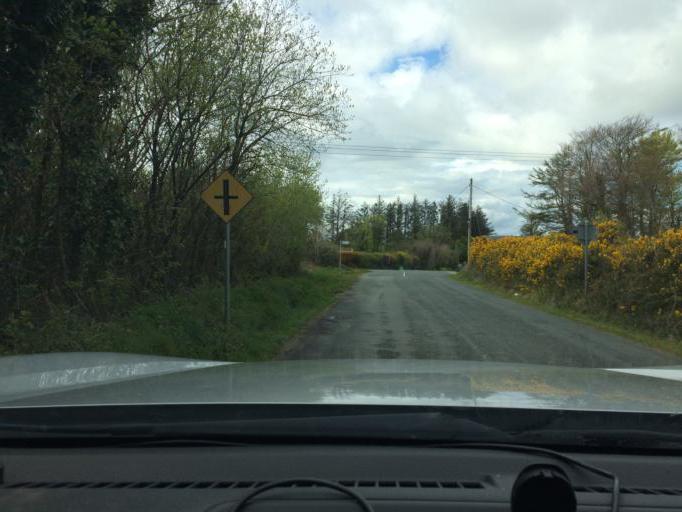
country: IE
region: Munster
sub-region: Waterford
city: Dungarvan
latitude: 52.0443
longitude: -7.6566
